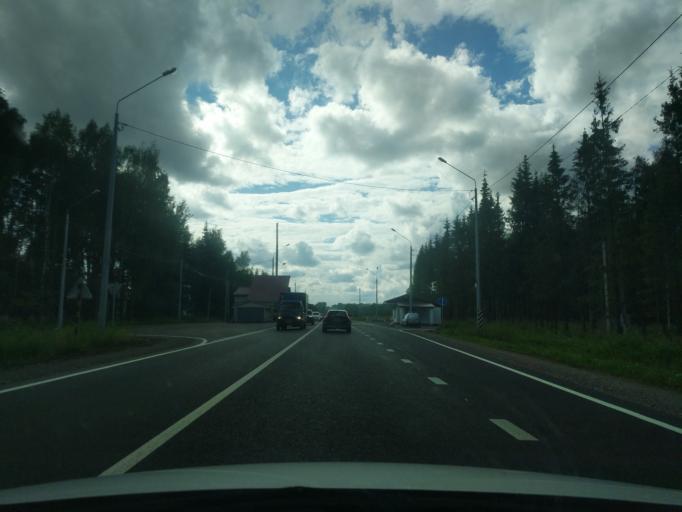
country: RU
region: Kostroma
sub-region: Kostromskoy Rayon
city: Kostroma
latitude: 57.7366
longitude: 40.8357
